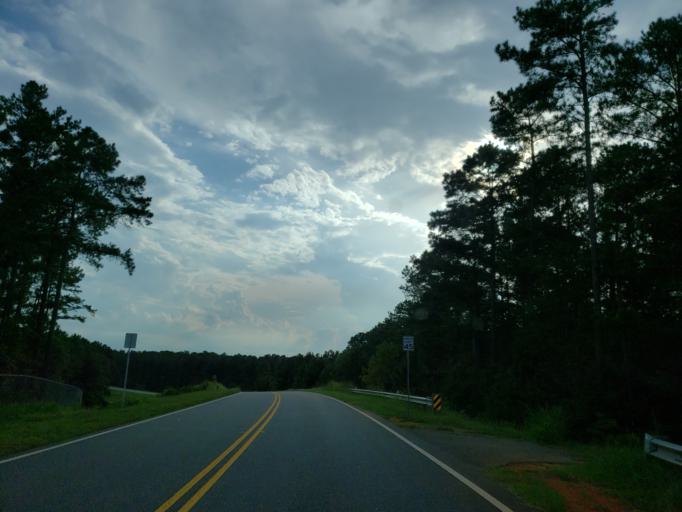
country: US
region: Georgia
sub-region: Bartow County
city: Euharlee
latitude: 34.1366
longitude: -84.9349
